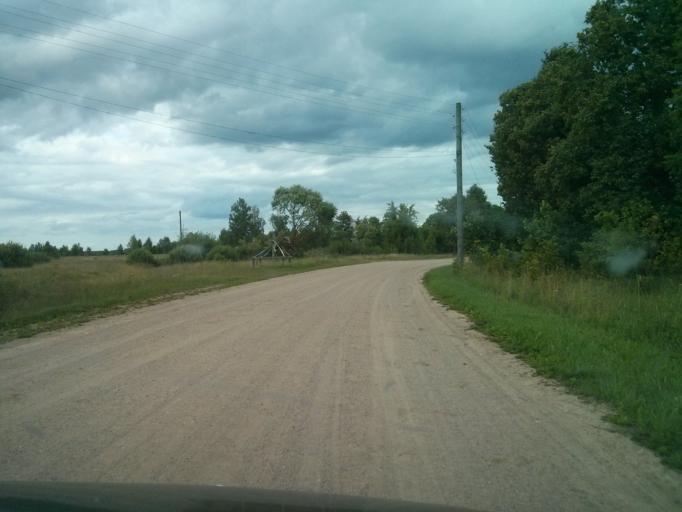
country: BY
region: Minsk
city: Plyeshchanitsy
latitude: 54.6043
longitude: 27.7900
